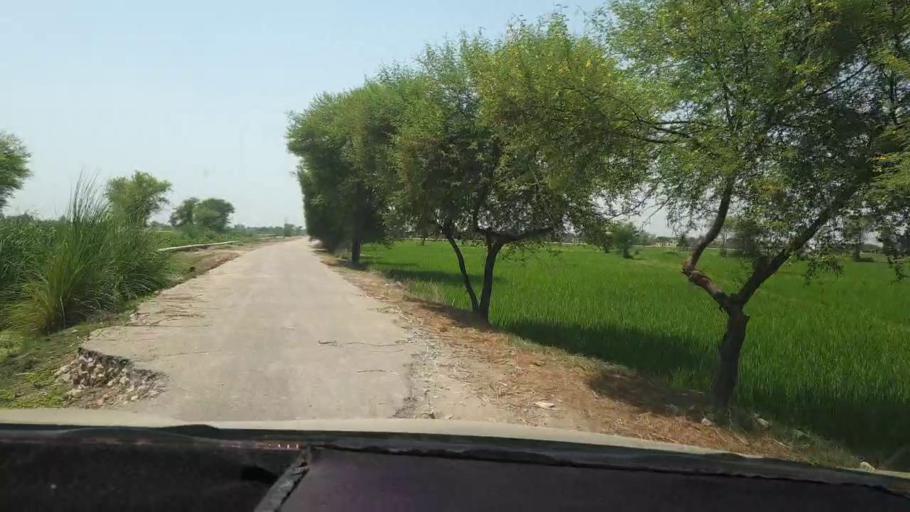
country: PK
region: Sindh
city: Shahdadkot
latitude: 27.8309
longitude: 67.9332
